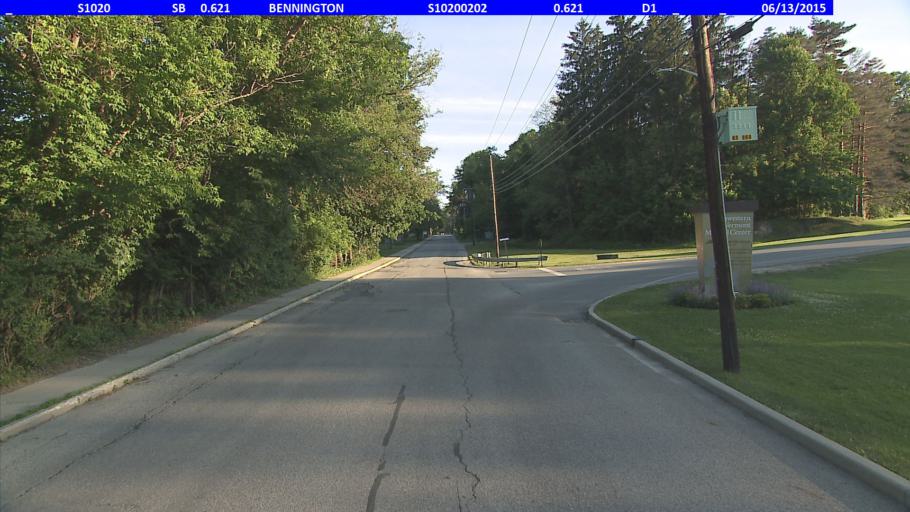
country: US
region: Vermont
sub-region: Bennington County
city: Bennington
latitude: 42.8742
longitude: -73.2042
